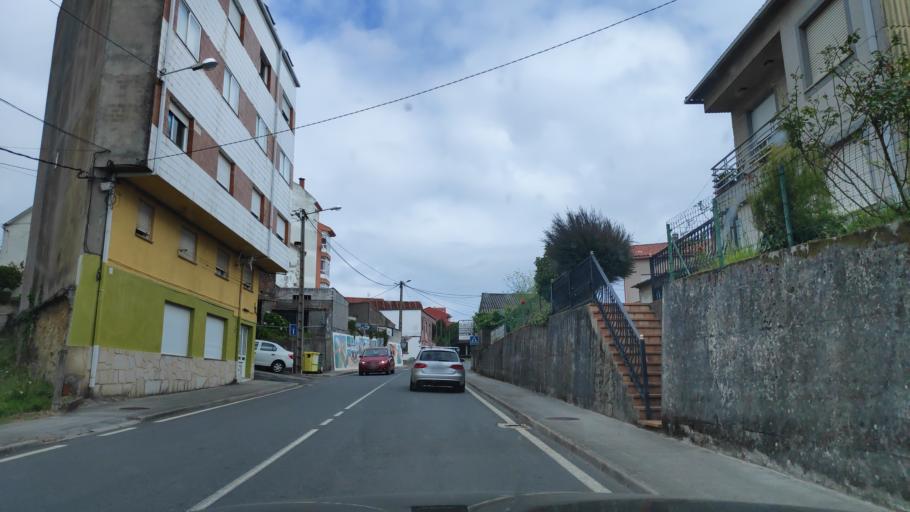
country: ES
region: Galicia
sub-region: Provincia da Coruna
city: Rianxo
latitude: 42.6487
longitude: -8.8139
